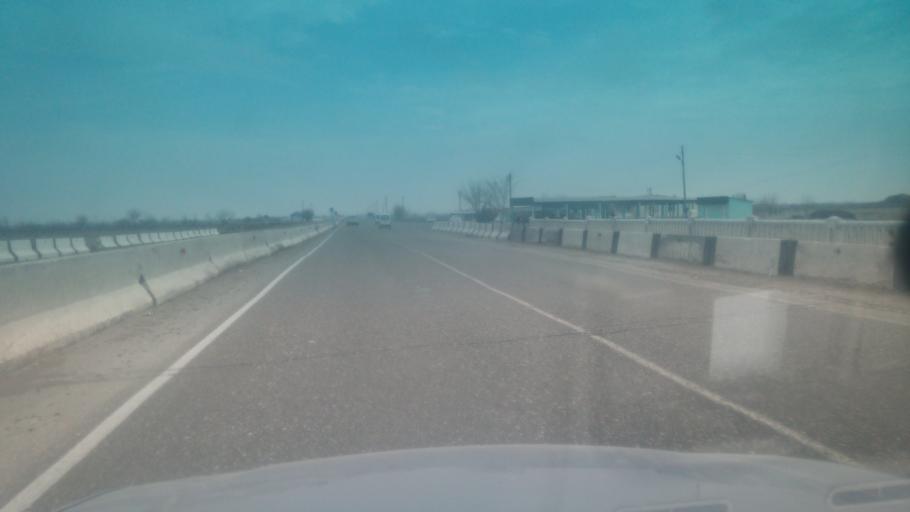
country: KZ
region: Ongtustik Qazaqstan
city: Myrzakent
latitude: 40.5023
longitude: 68.5334
